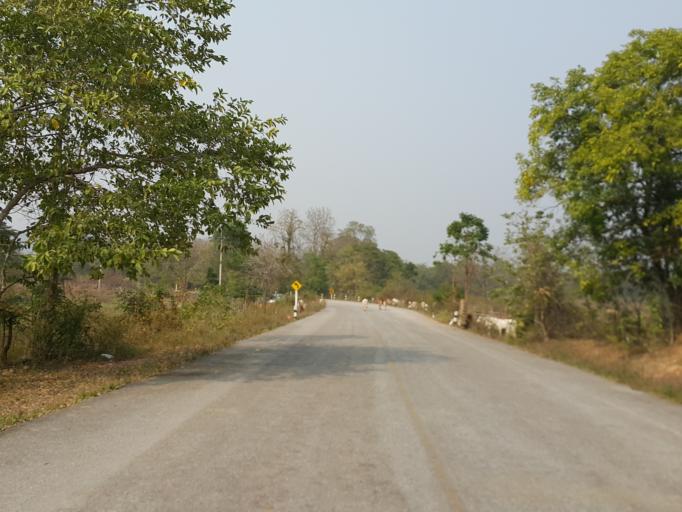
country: TH
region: Lampang
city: Mae Phrik
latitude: 17.4929
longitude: 99.0874
